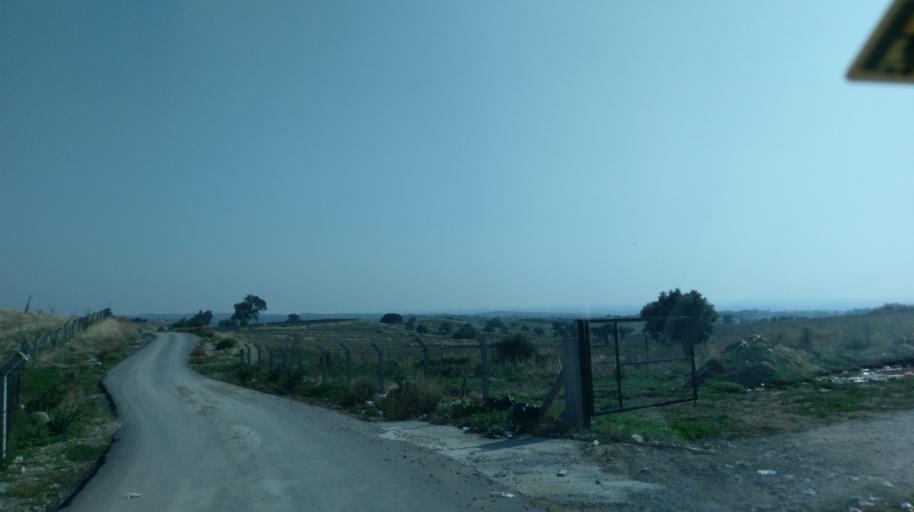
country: CY
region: Ammochostos
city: Lefkonoiko
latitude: 35.3078
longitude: 33.6333
